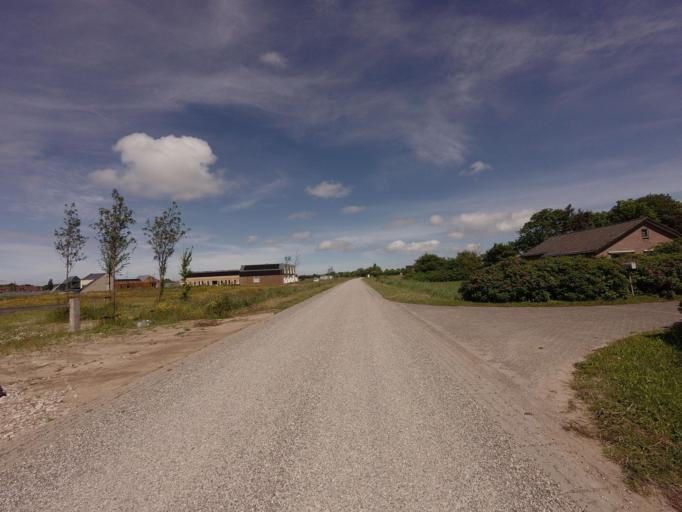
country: NL
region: North Holland
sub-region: Gemeente Texel
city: Den Burg
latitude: 53.0579
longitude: 4.8138
